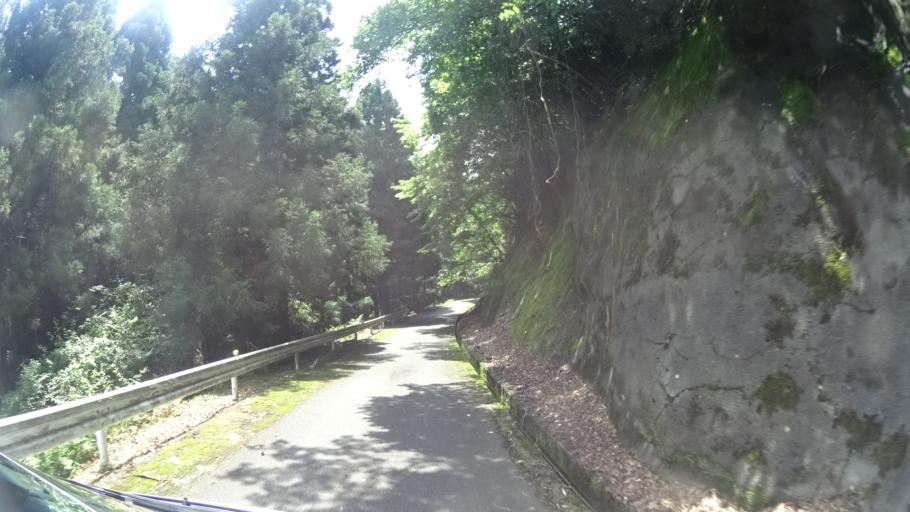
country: JP
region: Hyogo
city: Sasayama
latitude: 35.1675
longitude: 135.2013
